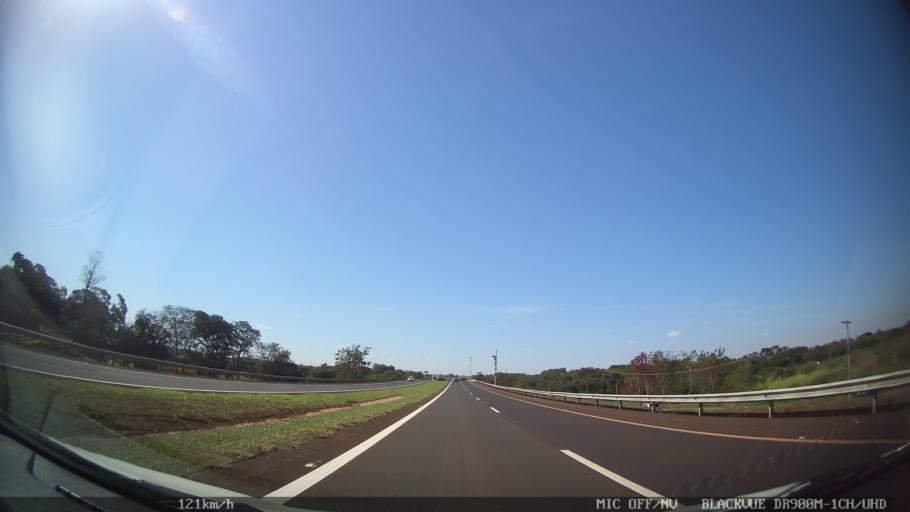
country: BR
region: Sao Paulo
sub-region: Ribeirao Preto
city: Ribeirao Preto
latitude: -21.1081
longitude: -47.8128
